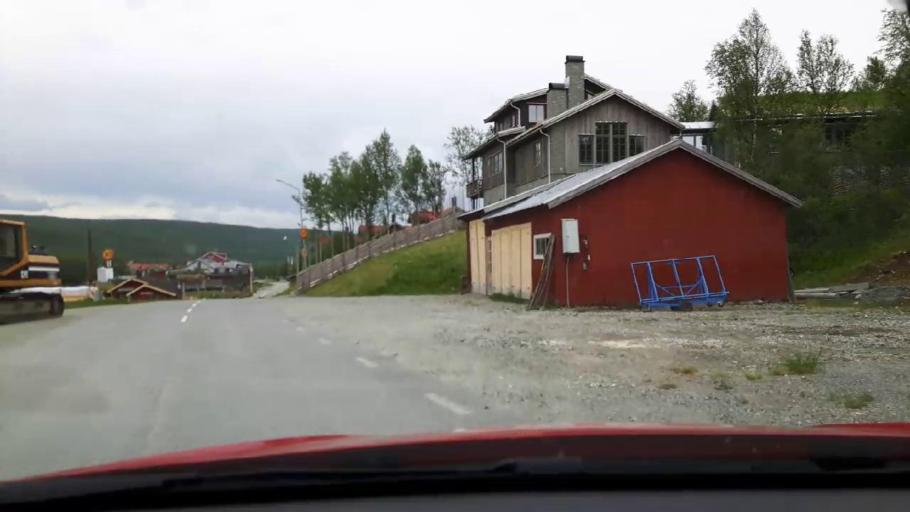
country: NO
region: Sor-Trondelag
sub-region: Tydal
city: Aas
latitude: 62.7031
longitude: 12.3847
